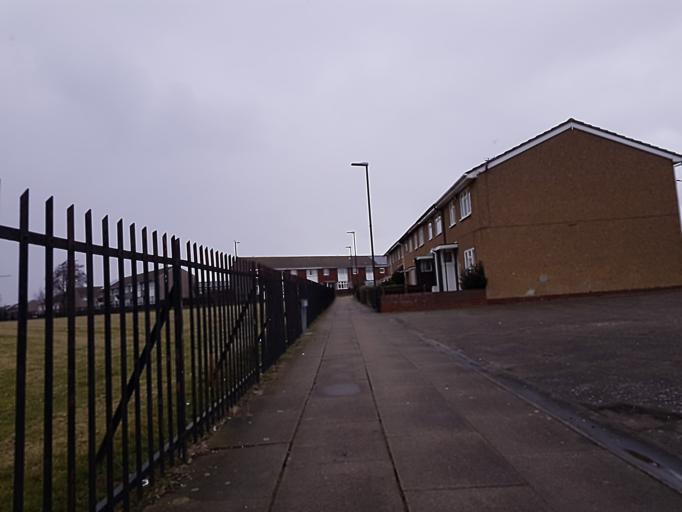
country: GB
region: England
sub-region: North East Lincolnshire
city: Great Coates
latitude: 53.5676
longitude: -0.1224
